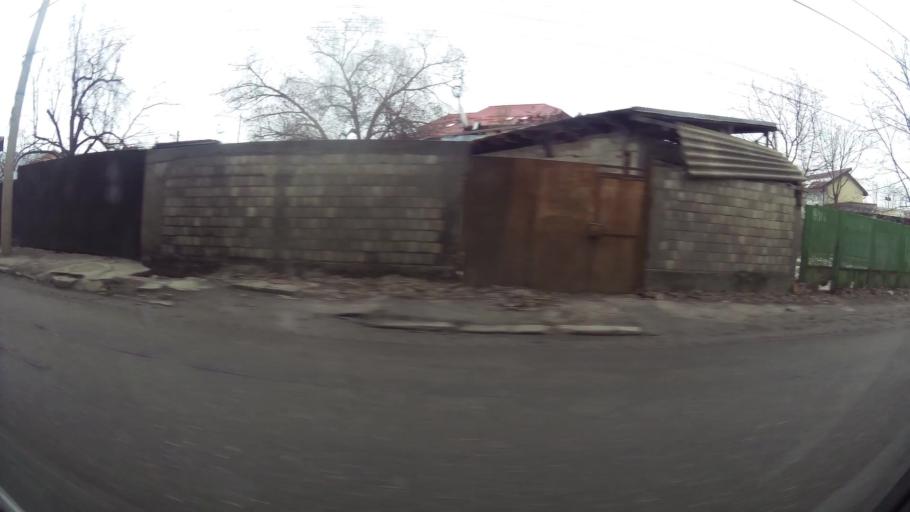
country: RO
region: Prahova
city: Ploiesti
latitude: 44.9424
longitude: 26.0481
